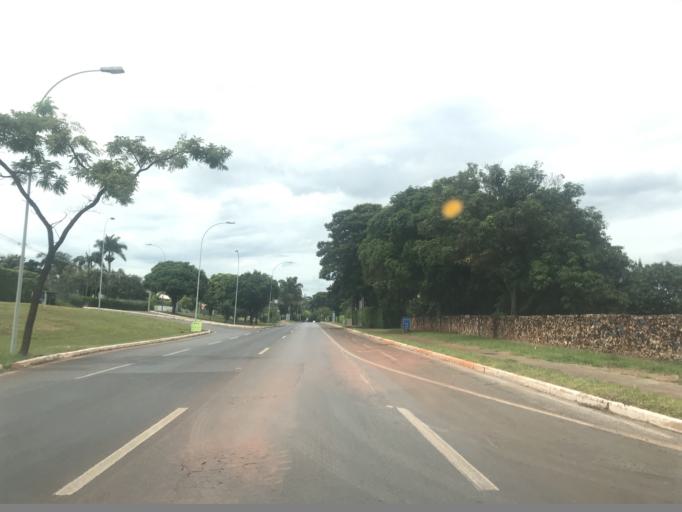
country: BR
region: Federal District
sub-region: Brasilia
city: Brasilia
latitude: -15.8364
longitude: -47.8361
